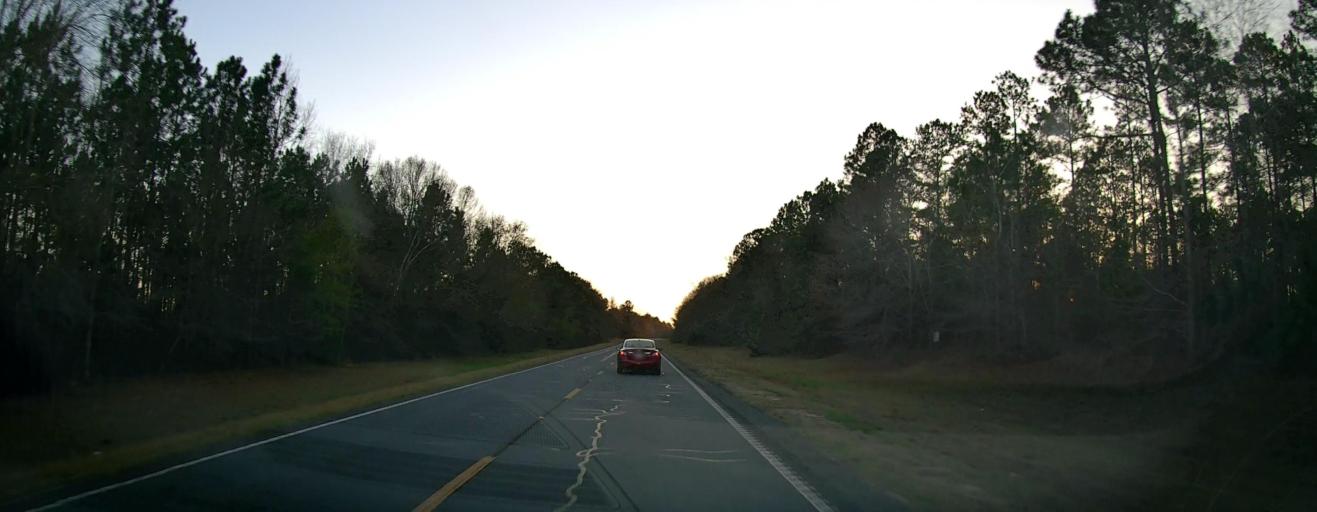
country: US
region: Georgia
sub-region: Dodge County
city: Eastman
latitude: 32.2689
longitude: -83.1237
